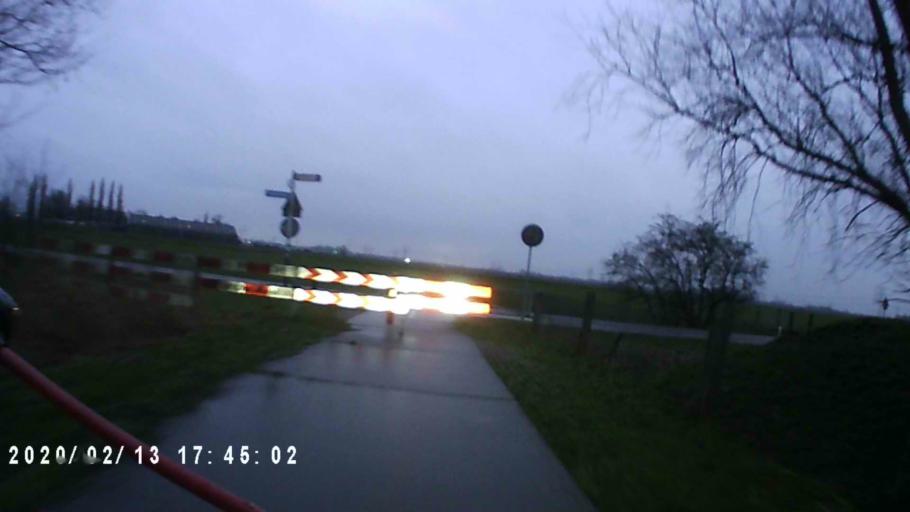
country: NL
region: Groningen
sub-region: Gemeente Zuidhorn
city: Aduard
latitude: 53.2294
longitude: 6.4795
